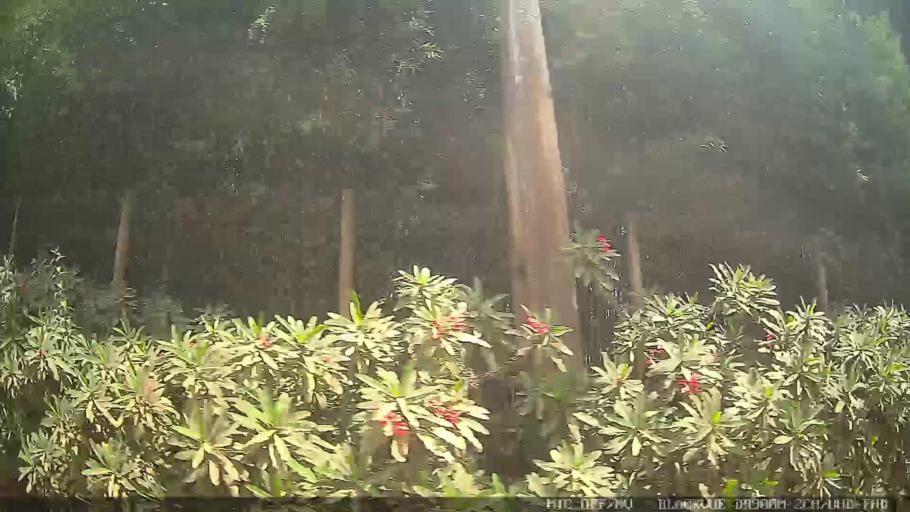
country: BR
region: Sao Paulo
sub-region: Atibaia
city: Atibaia
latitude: -23.1559
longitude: -46.6190
